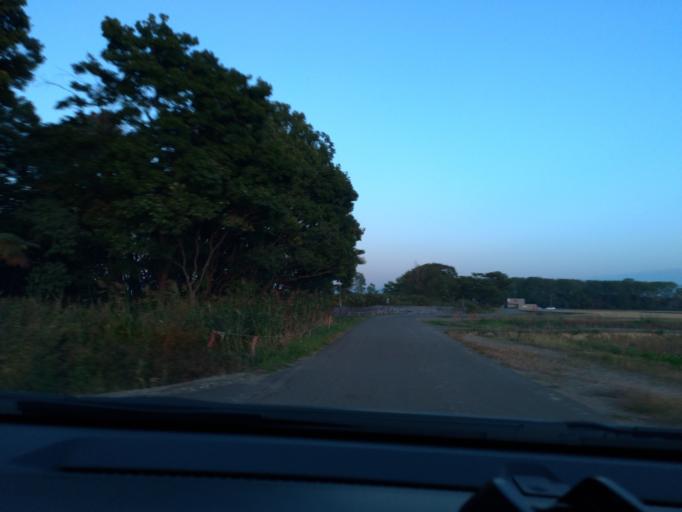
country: JP
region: Hokkaido
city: Iwamizawa
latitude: 43.3300
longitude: 141.7097
